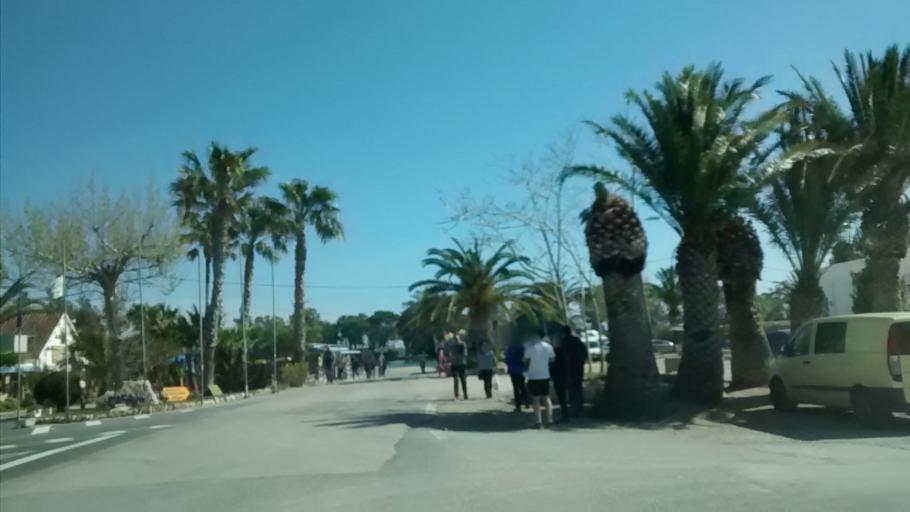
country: ES
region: Catalonia
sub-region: Provincia de Tarragona
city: Deltebre
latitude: 40.7136
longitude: 0.8342
